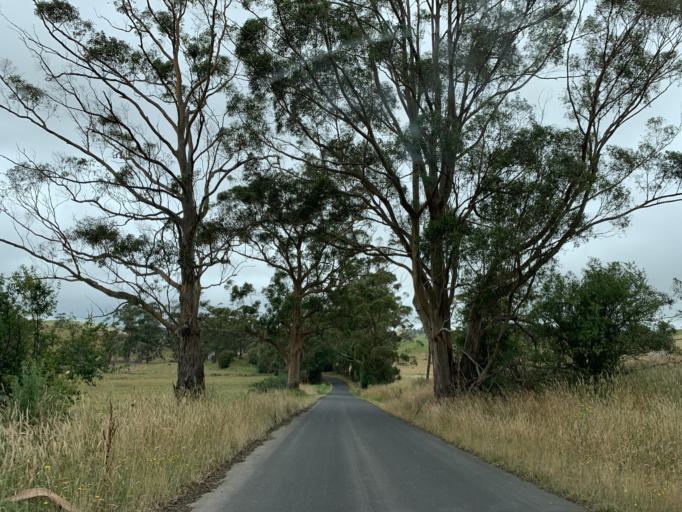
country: AU
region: Victoria
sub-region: Baw Baw
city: Warragul
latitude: -38.2946
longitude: 145.8463
